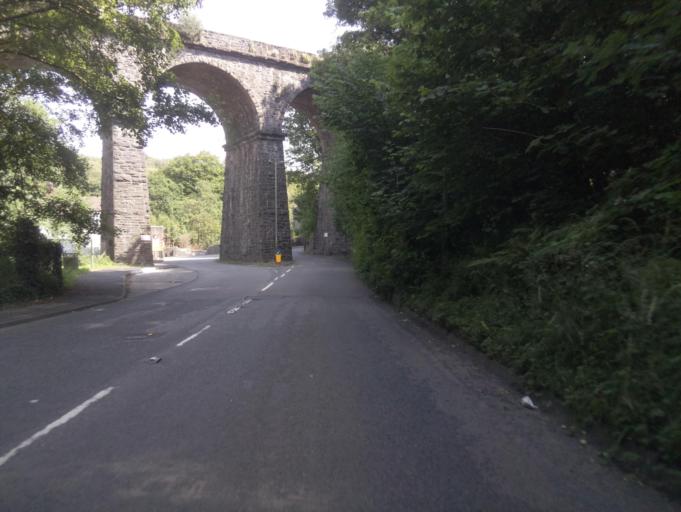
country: GB
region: Wales
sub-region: Caerphilly County Borough
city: Bargoed
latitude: 51.6948
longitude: -3.2320
